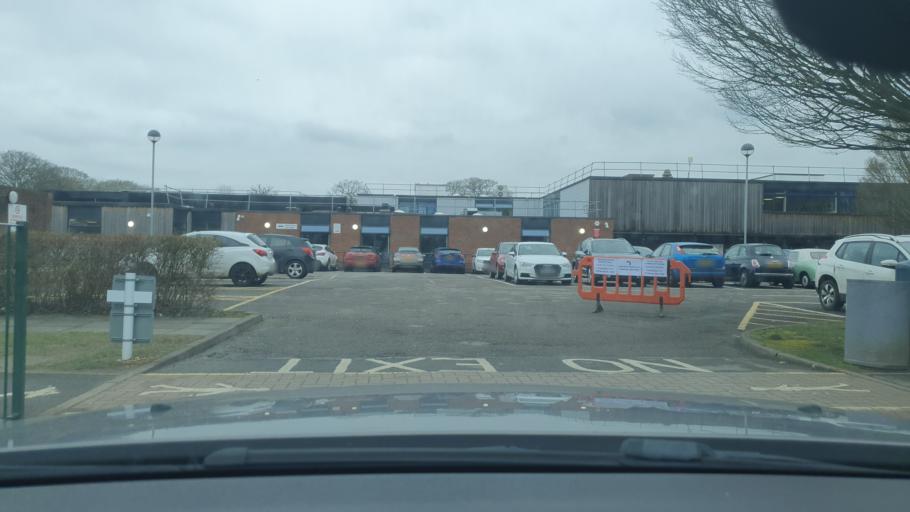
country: GB
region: England
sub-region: West Berkshire
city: Tilehurst
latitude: 51.4714
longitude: -1.0548
